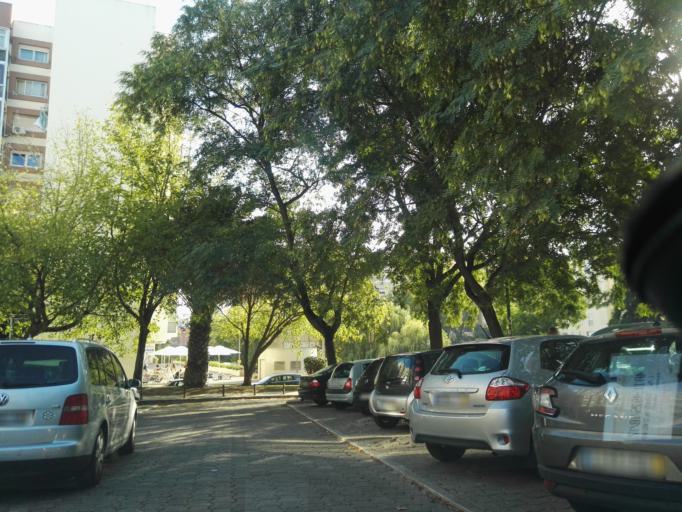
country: PT
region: Lisbon
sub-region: Odivelas
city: Olival do Basto
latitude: 38.7639
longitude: -9.1534
